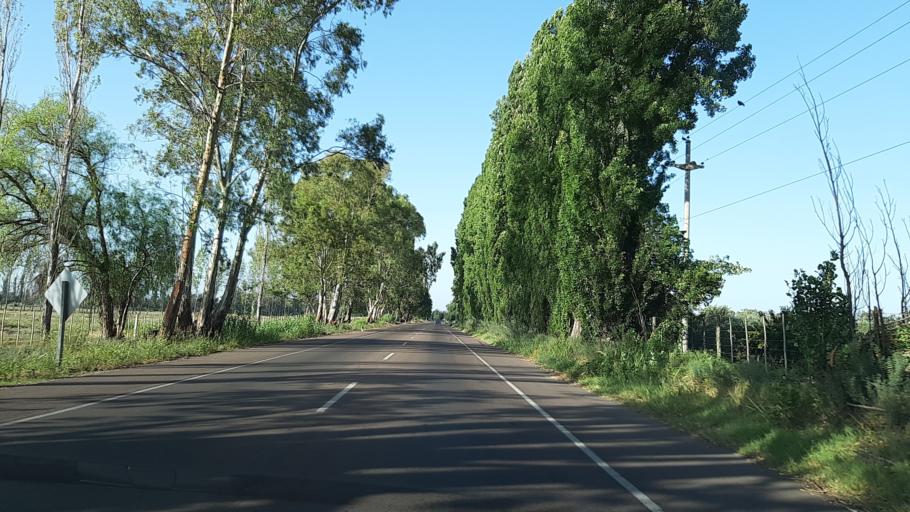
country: AR
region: Mendoza
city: San Martin
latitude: -32.9583
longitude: -68.4368
